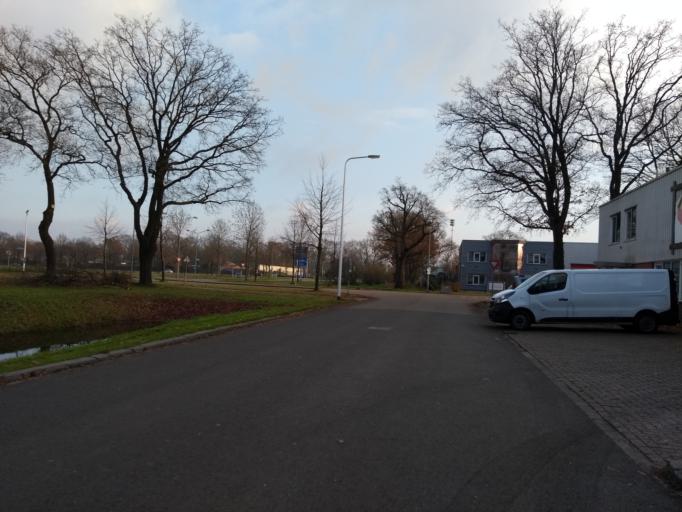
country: NL
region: Overijssel
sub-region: Gemeente Almelo
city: Almelo
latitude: 52.3749
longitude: 6.6492
